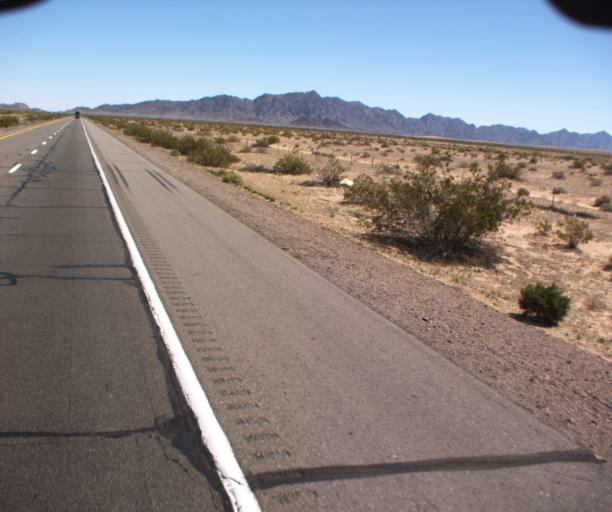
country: US
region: Arizona
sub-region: Yuma County
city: Wellton
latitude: 32.7131
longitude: -113.8231
